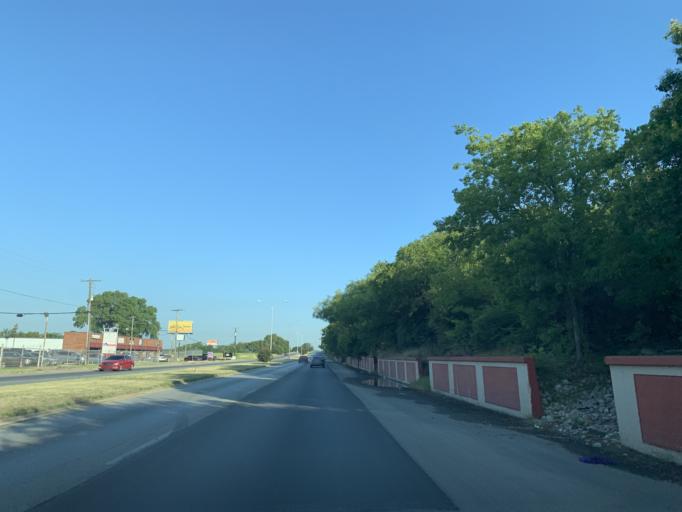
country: US
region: Texas
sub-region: Tarrant County
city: River Oaks
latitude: 32.7709
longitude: -97.3603
